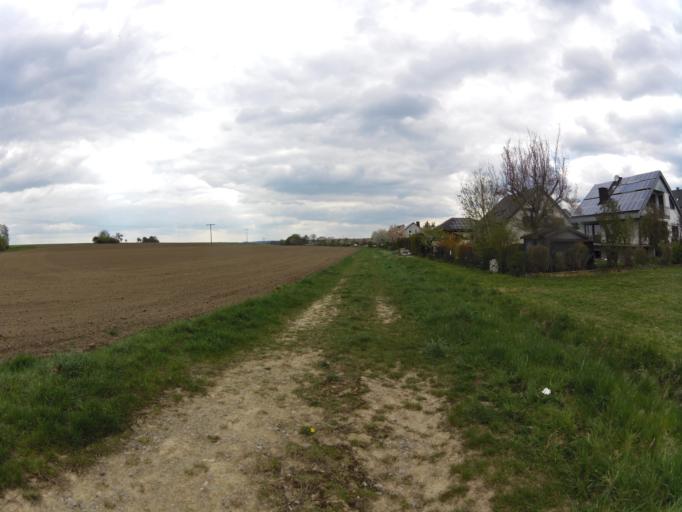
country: DE
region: Bavaria
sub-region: Regierungsbezirk Unterfranken
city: Giebelstadt
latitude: 49.6513
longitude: 9.9412
